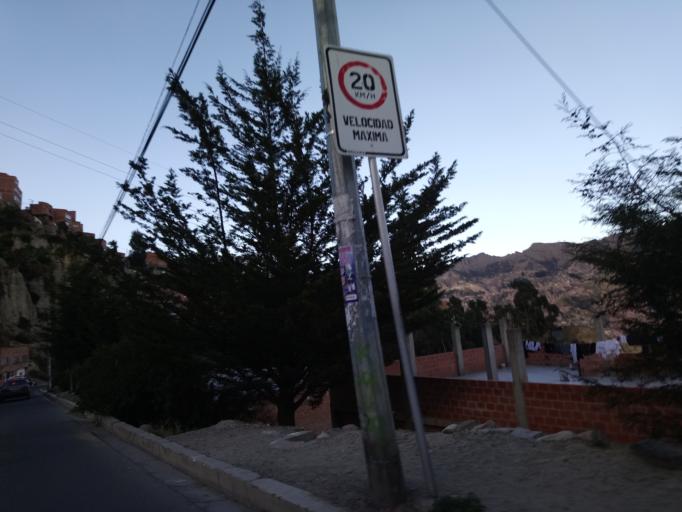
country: BO
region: La Paz
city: La Paz
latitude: -16.4871
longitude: -68.1281
